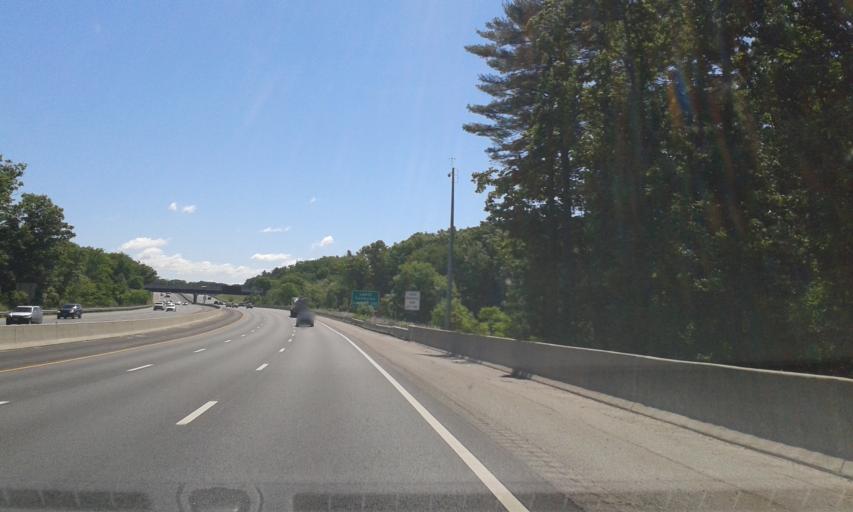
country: US
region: Massachusetts
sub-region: Middlesex County
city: Chelmsford
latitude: 42.6203
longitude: -71.3565
